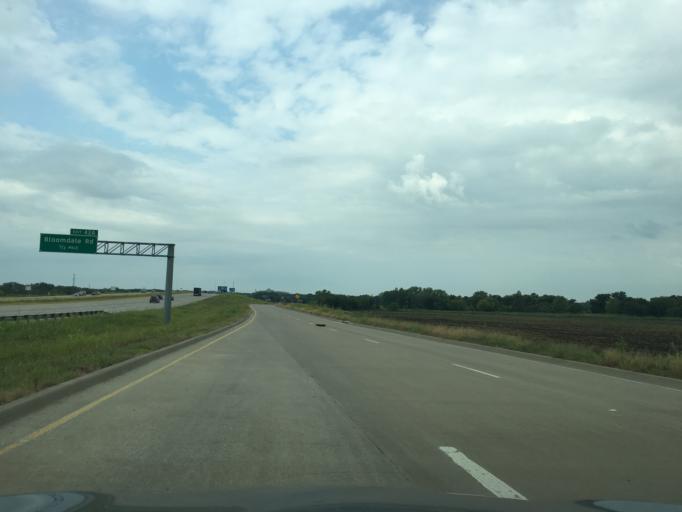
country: US
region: Texas
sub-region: Collin County
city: Melissa
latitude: 33.2544
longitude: -96.6137
